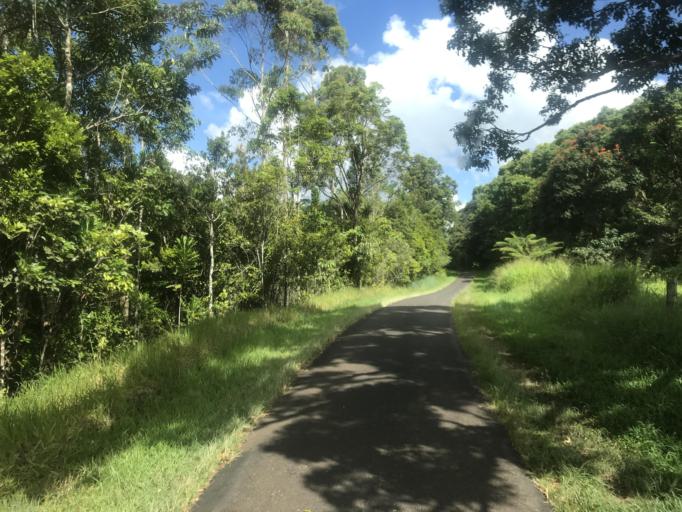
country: AU
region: Queensland
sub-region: Tablelands
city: Ravenshoe
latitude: -17.5456
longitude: 145.6951
